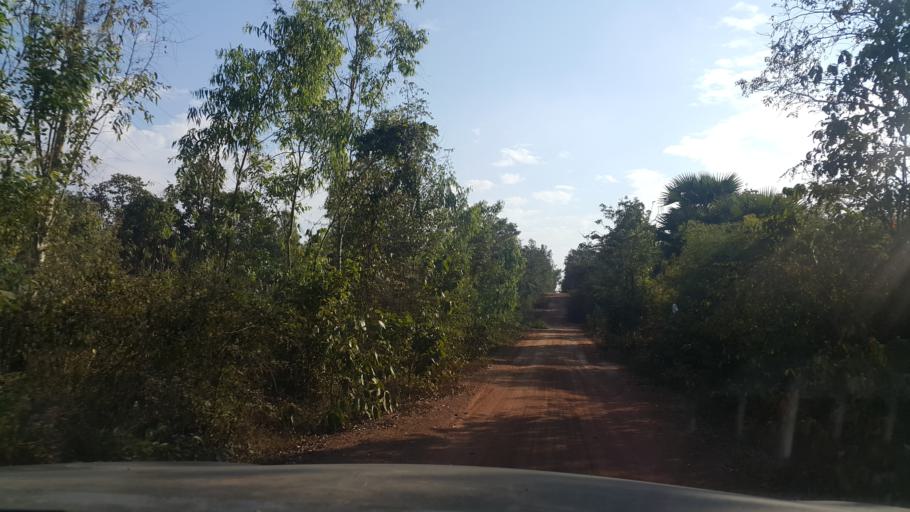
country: TH
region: Lampang
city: Hang Chat
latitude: 18.2821
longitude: 99.3574
